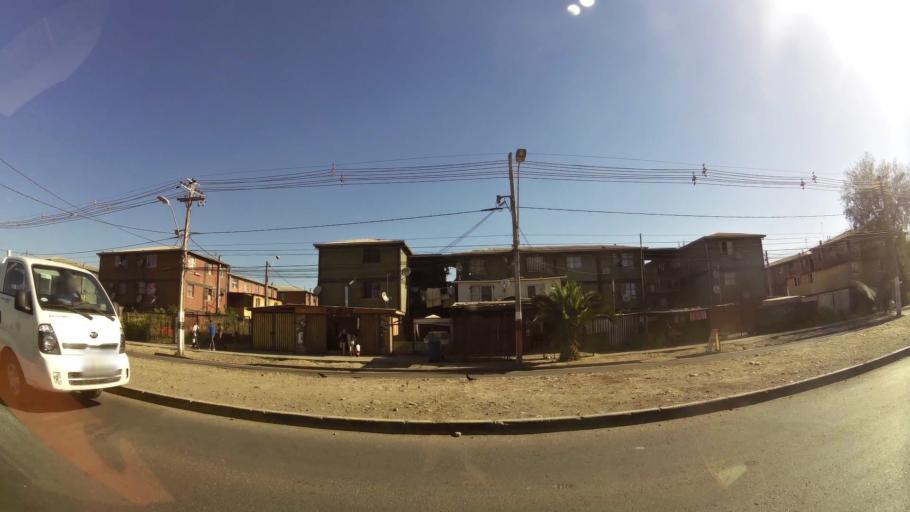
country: CL
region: Santiago Metropolitan
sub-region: Provincia de Maipo
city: San Bernardo
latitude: -33.5947
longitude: -70.6750
